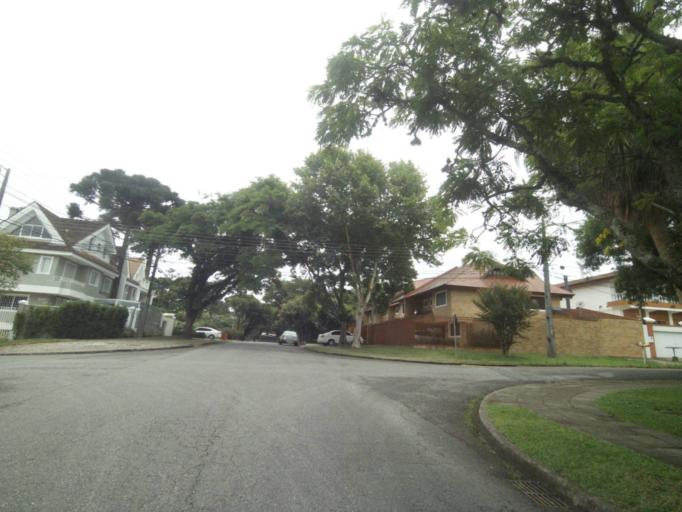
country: BR
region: Parana
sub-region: Curitiba
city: Curitiba
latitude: -25.4108
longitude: -49.2833
